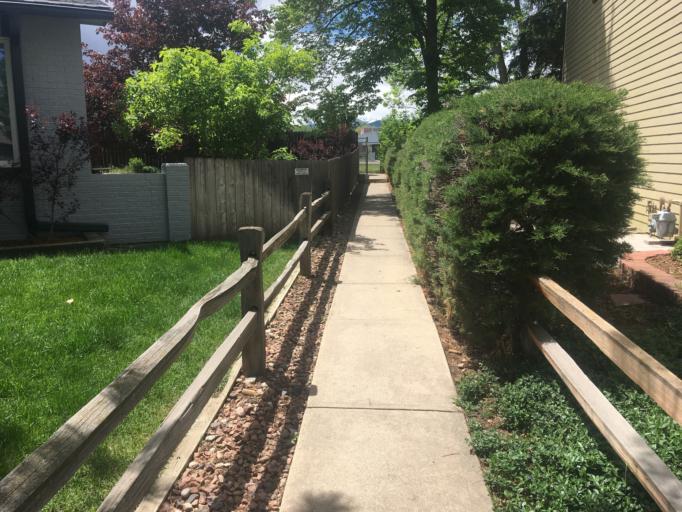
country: US
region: Colorado
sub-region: Boulder County
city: Boulder
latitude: 40.0078
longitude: -105.2323
